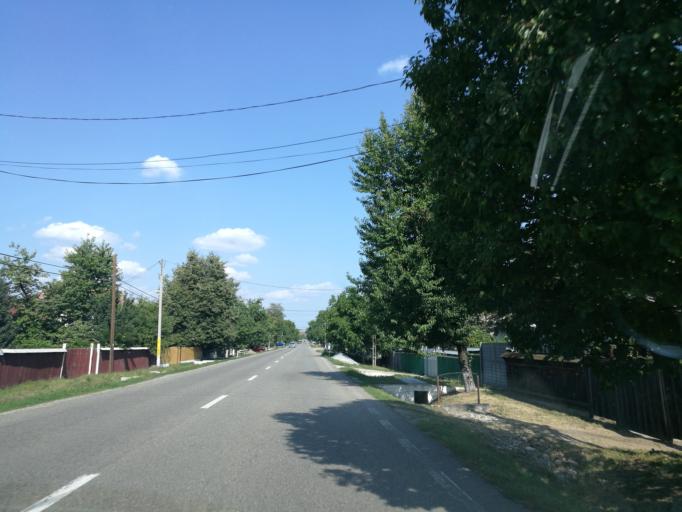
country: RO
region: Neamt
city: Bodesti
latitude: 47.0401
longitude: 26.4078
